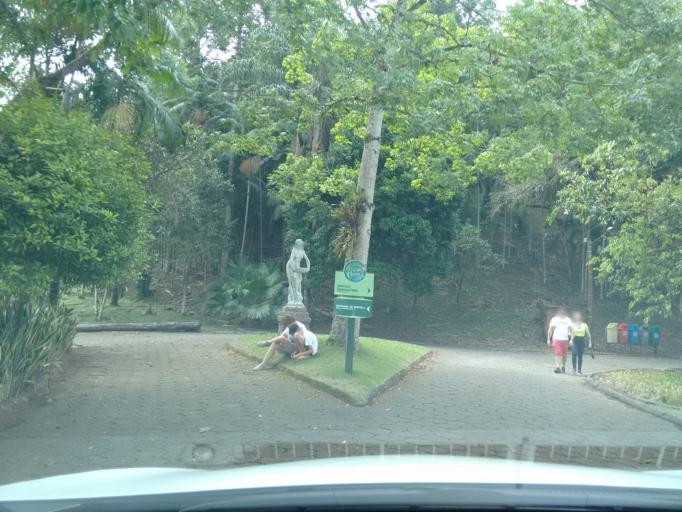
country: BR
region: Santa Catarina
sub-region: Jaragua Do Sul
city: Jaragua do Sul
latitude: -26.5062
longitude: -49.1295
